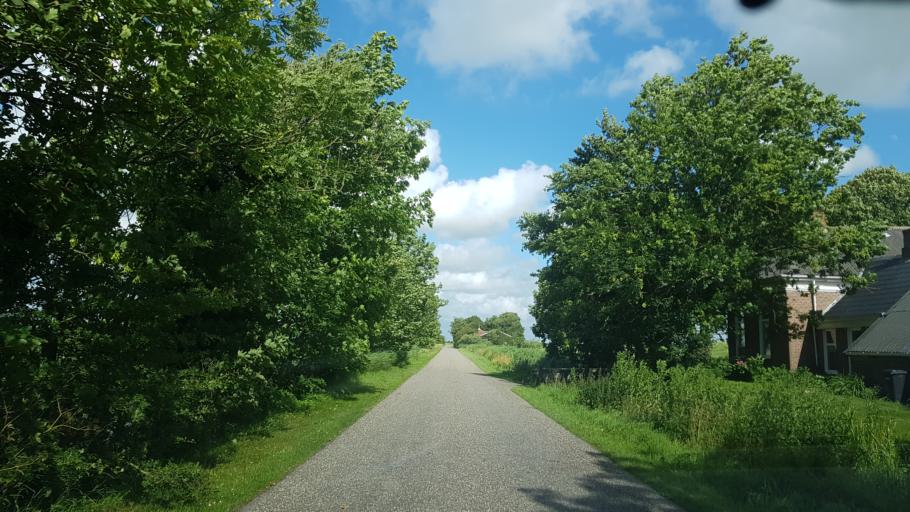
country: NL
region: Groningen
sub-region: Gemeente Winsum
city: Winsum
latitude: 53.4069
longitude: 6.5494
